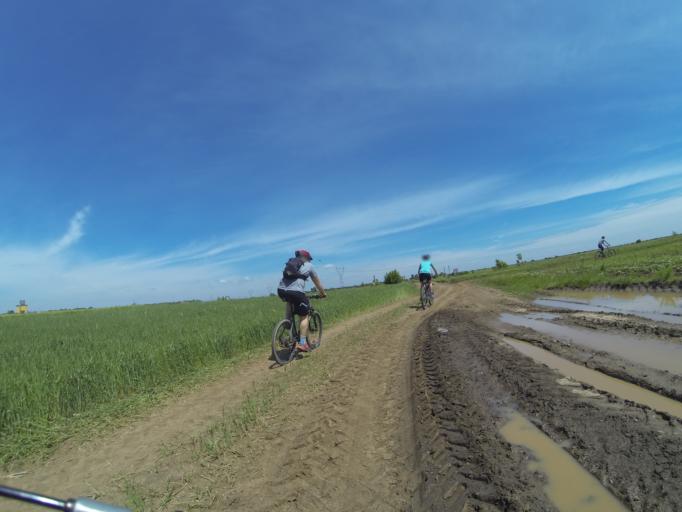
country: RO
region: Dolj
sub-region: Comuna Leu
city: Leu
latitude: 44.1900
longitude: 24.0468
